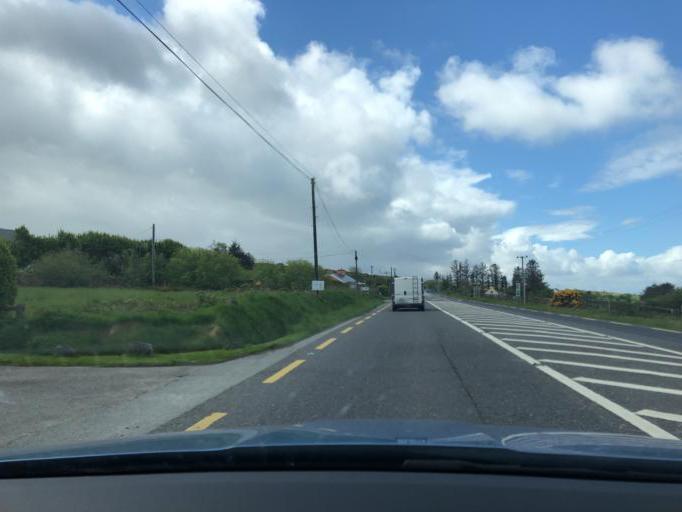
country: IE
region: Munster
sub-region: Ciarrai
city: Tralee
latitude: 52.3232
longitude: -9.6479
